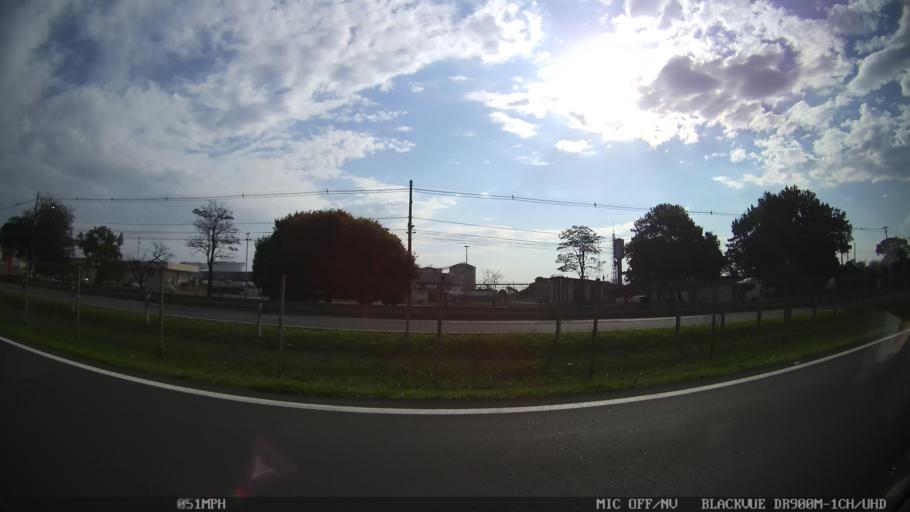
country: BR
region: Sao Paulo
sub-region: Paulinia
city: Paulinia
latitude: -22.7246
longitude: -47.1447
